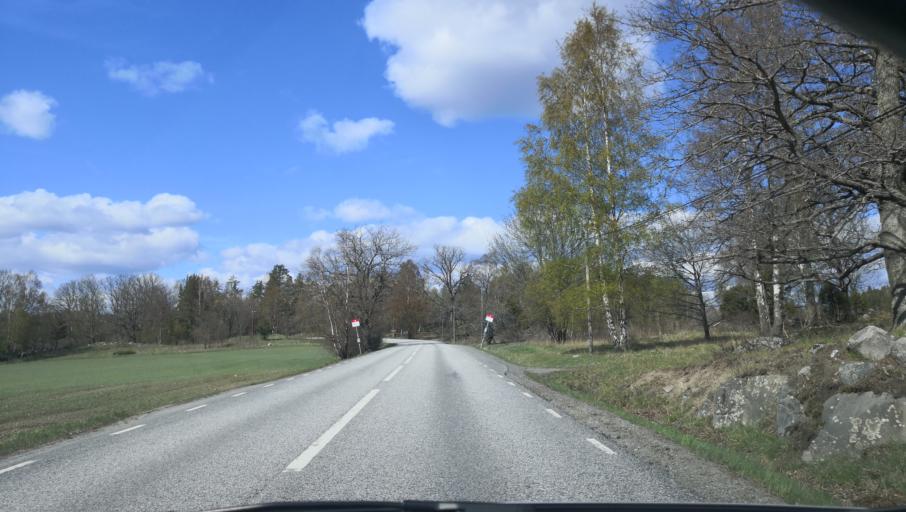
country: SE
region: Stockholm
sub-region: Varmdo Kommun
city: Hemmesta
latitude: 59.3765
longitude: 18.5262
